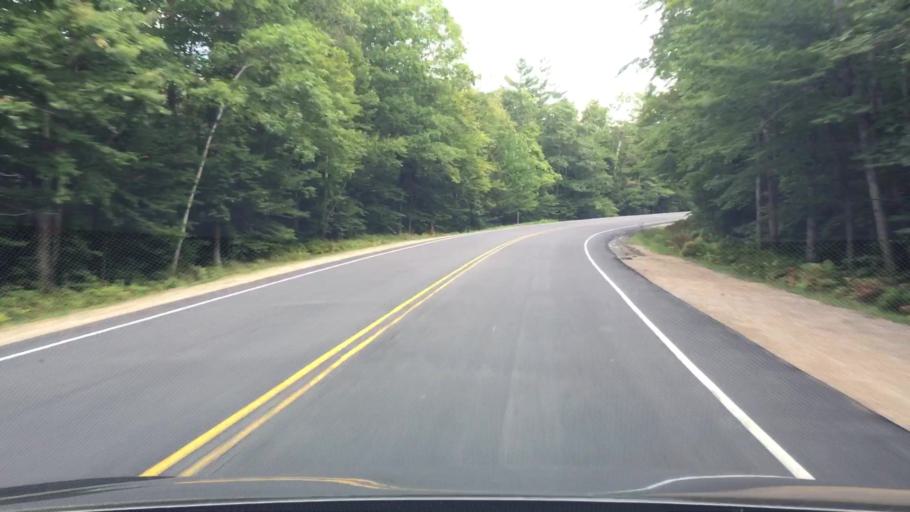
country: US
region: New Hampshire
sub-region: Carroll County
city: Conway
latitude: 44.0007
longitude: -71.2317
